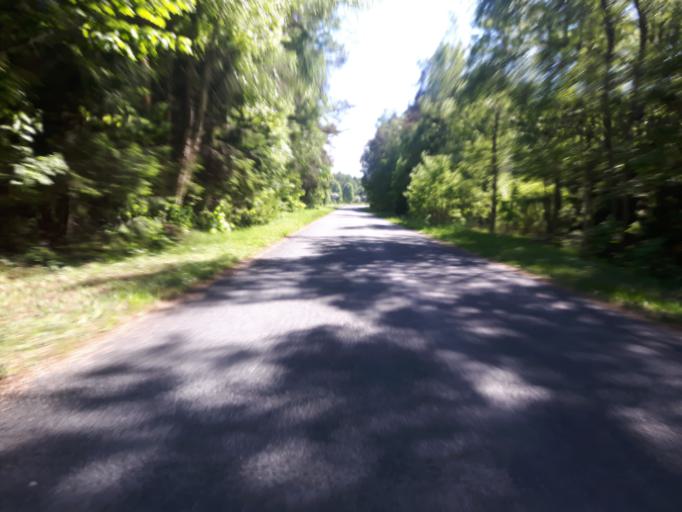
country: EE
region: Laeaene-Virumaa
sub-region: Haljala vald
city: Haljala
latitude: 59.5757
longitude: 26.2682
